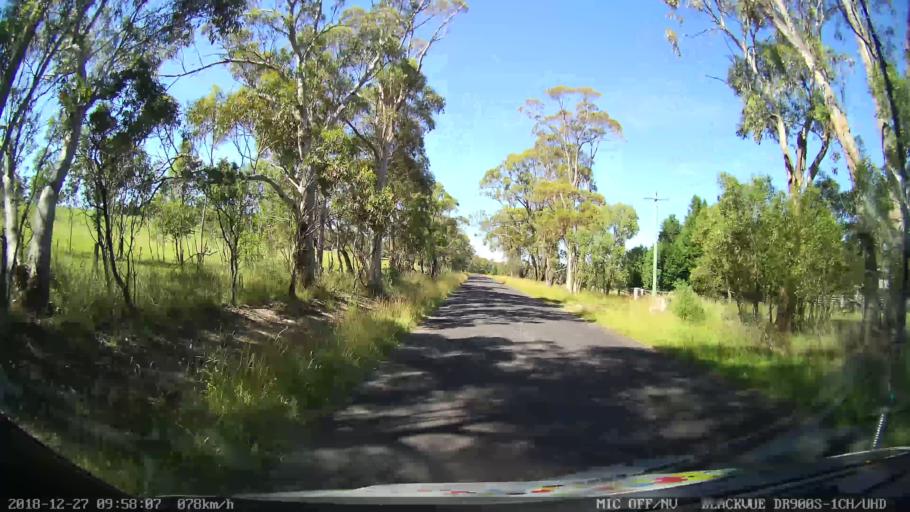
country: AU
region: New South Wales
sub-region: Lithgow
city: Portland
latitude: -33.4272
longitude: 149.9668
